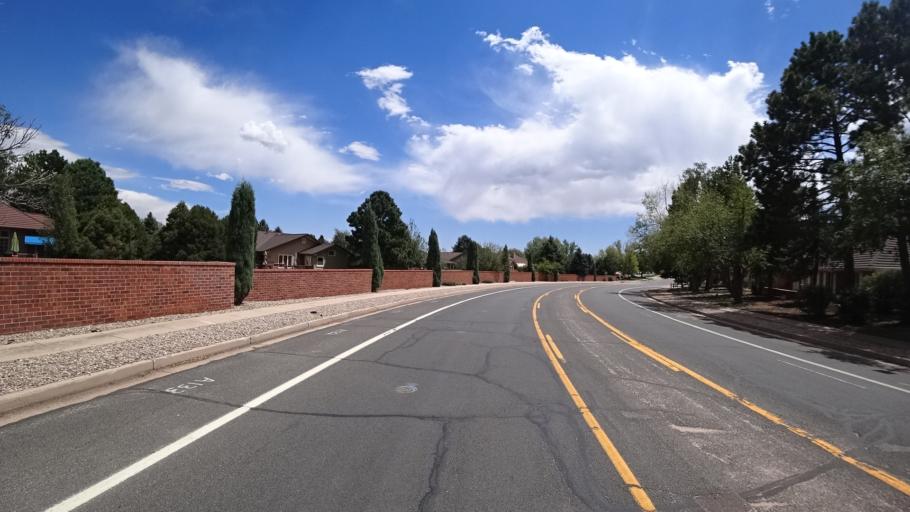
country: US
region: Colorado
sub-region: El Paso County
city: Colorado Springs
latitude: 38.7913
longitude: -104.8262
